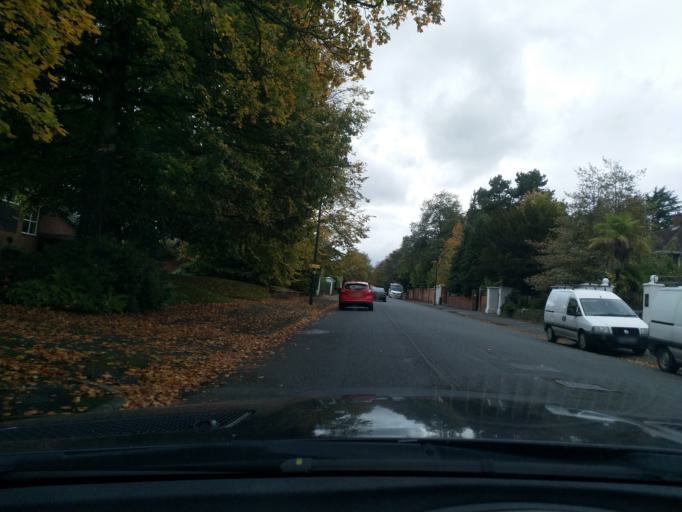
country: GB
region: England
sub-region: City and Borough of Birmingham
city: Birmingham
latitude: 52.4633
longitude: -1.9085
